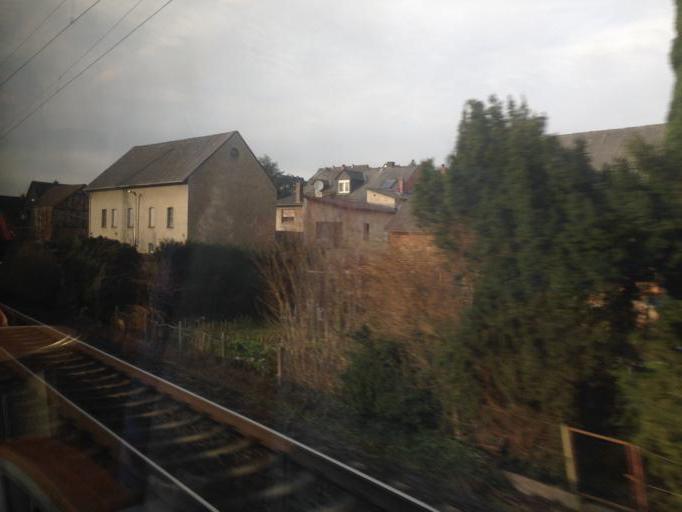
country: DE
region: Hesse
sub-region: Regierungsbezirk Giessen
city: Asslar
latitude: 50.5871
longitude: 8.4673
